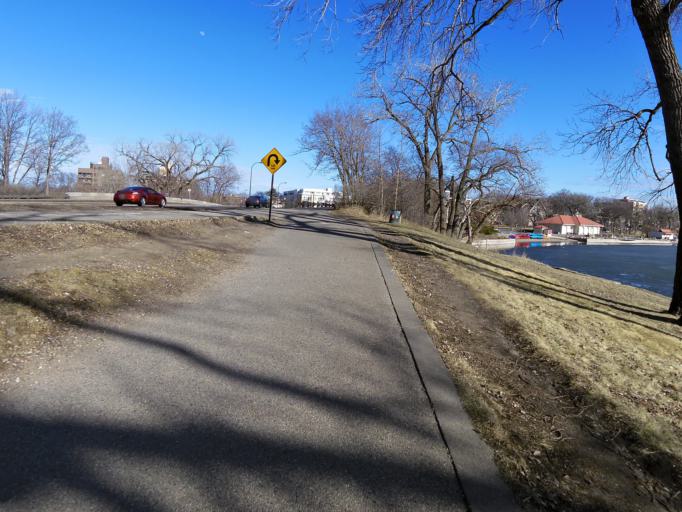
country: US
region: Minnesota
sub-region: Hennepin County
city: Saint Louis Park
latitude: 44.9496
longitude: -93.3082
